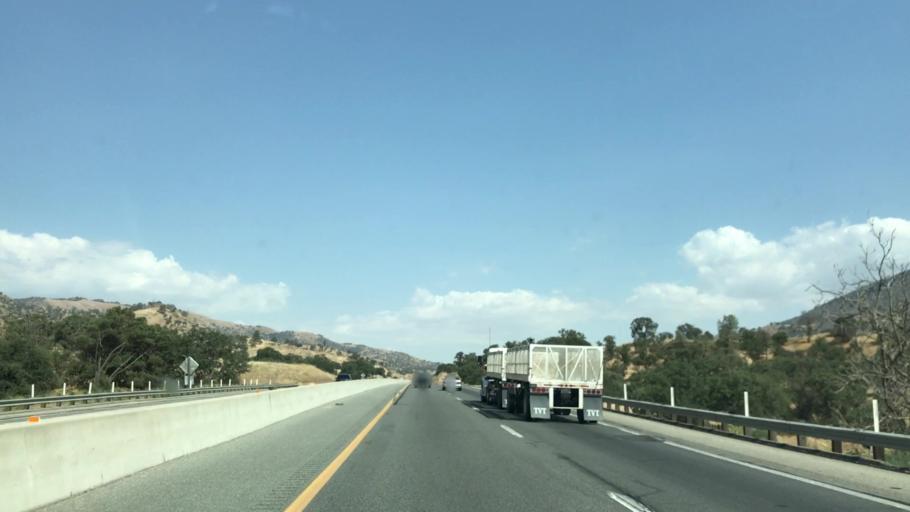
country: US
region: California
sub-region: Kern County
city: Golden Hills
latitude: 35.2143
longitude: -118.5498
